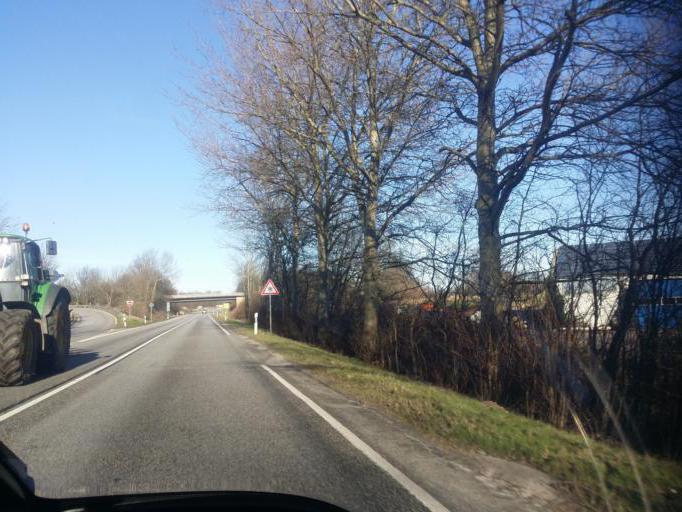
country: DE
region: Schleswig-Holstein
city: Tonning
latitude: 54.3224
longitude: 8.9551
